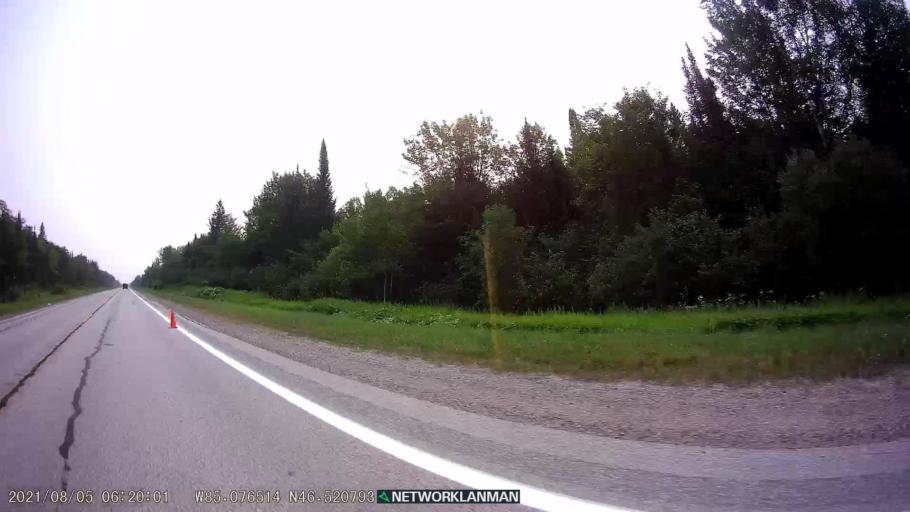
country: US
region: Michigan
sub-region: Luce County
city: Newberry
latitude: 46.5222
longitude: -85.0746
